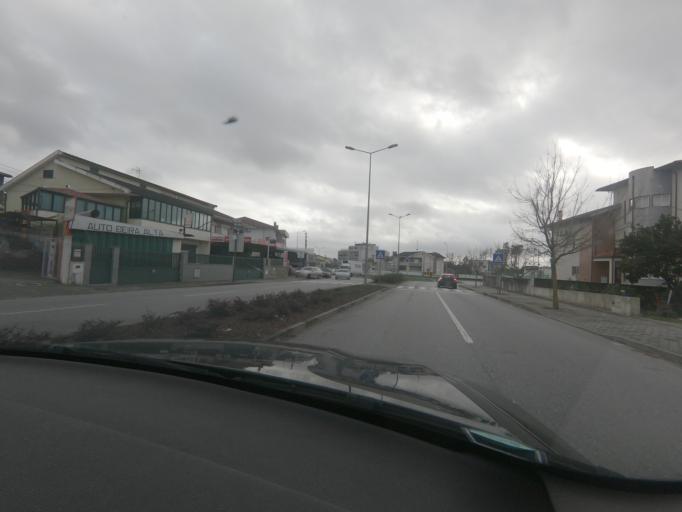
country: PT
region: Viseu
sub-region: Viseu
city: Abraveses
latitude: 40.6863
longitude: -7.9276
